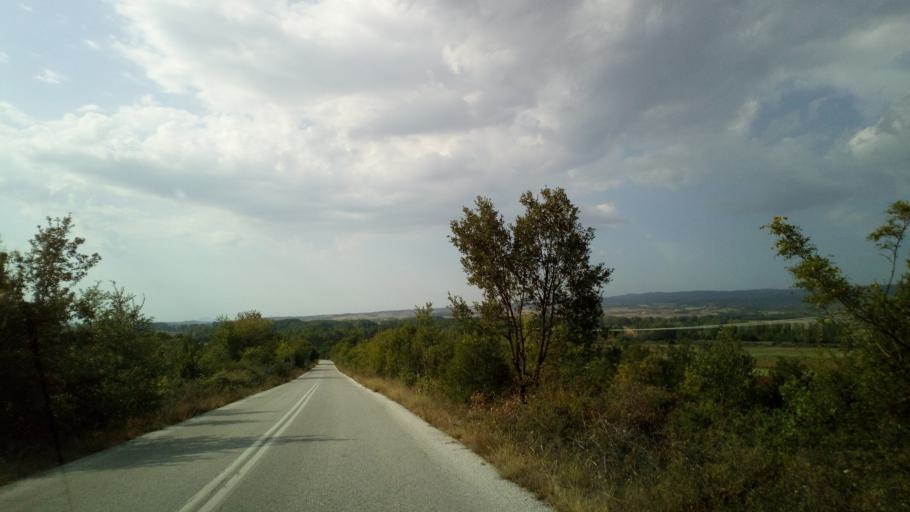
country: GR
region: Central Macedonia
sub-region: Nomos Chalkidikis
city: Galatista
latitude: 40.5505
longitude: 23.3223
